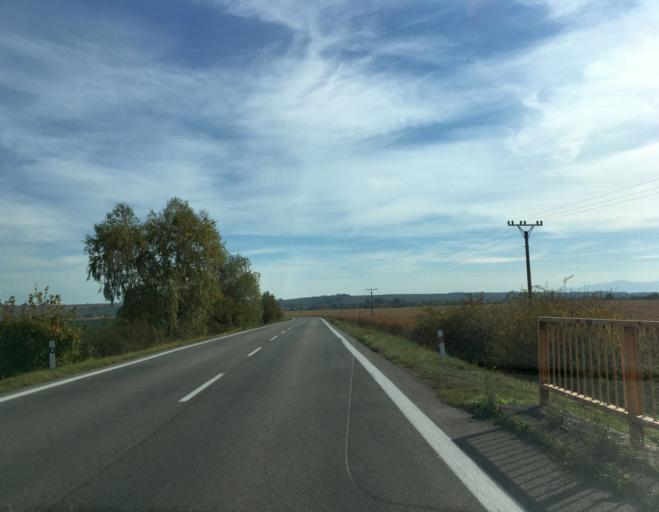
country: SK
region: Nitriansky
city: Zeliezovce
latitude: 48.1249
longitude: 18.6801
